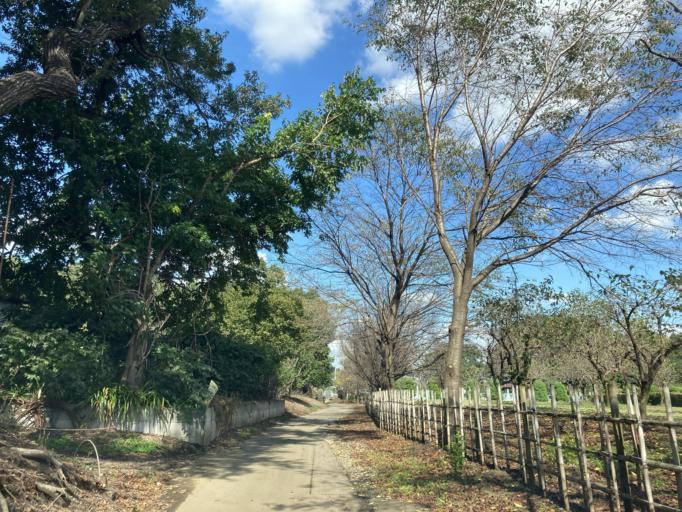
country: JP
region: Saitama
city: Tokorozawa
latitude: 35.8067
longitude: 139.5018
